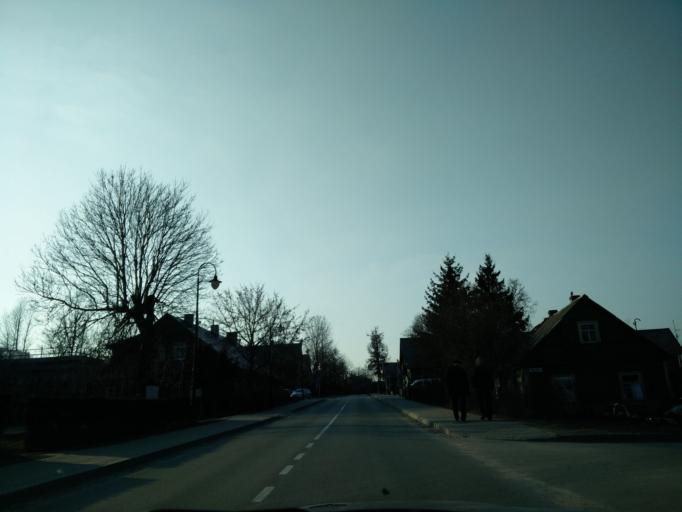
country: LT
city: Trakai
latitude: 54.6505
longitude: 24.9249
